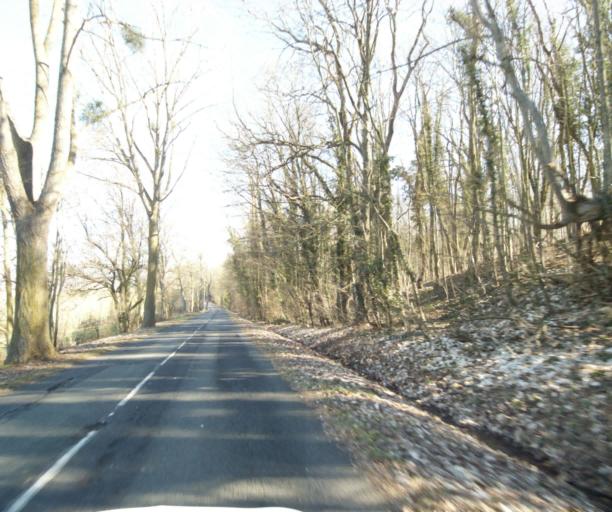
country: FR
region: Lorraine
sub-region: Departement de Meurthe-et-Moselle
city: Lay-Saint-Christophe
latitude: 48.7363
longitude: 6.1856
